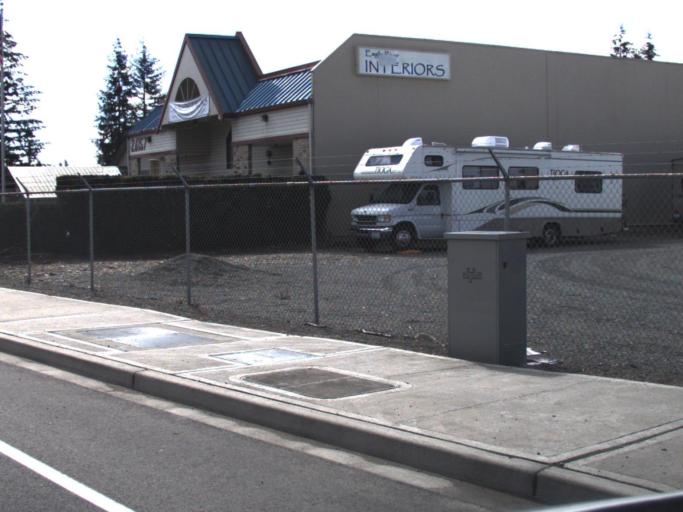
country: US
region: Washington
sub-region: King County
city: Maple Valley
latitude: 47.3675
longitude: -122.0222
